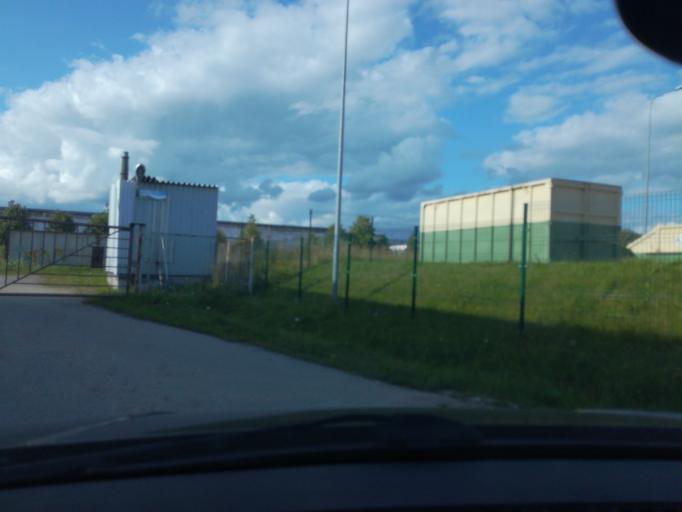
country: LT
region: Alytaus apskritis
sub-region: Alytus
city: Alytus
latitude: 54.4177
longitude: 24.0128
